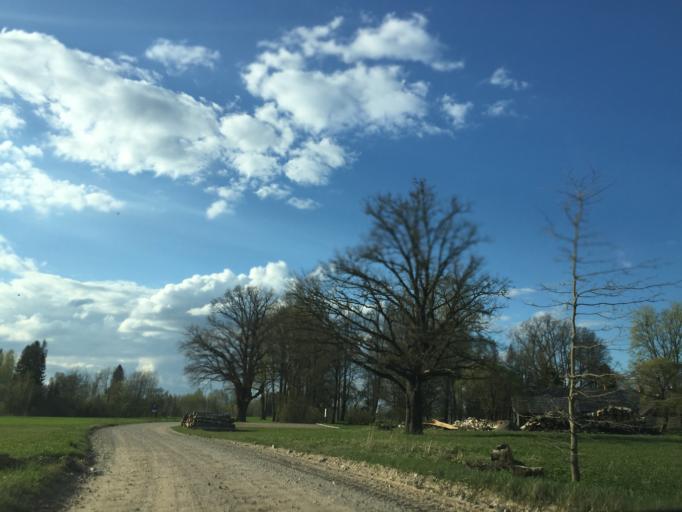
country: LV
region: Beverina
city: Murmuiza
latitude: 57.3948
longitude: 25.4781
